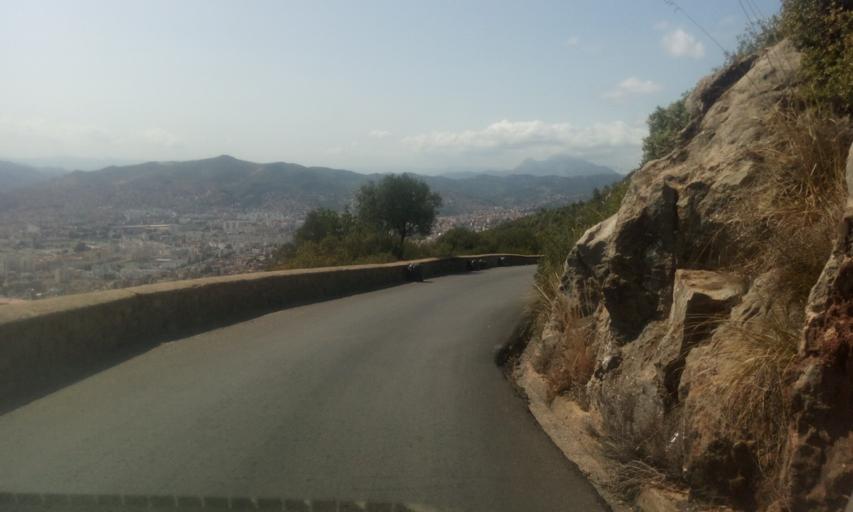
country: DZ
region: Bejaia
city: Bejaia
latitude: 36.7631
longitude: 5.0888
